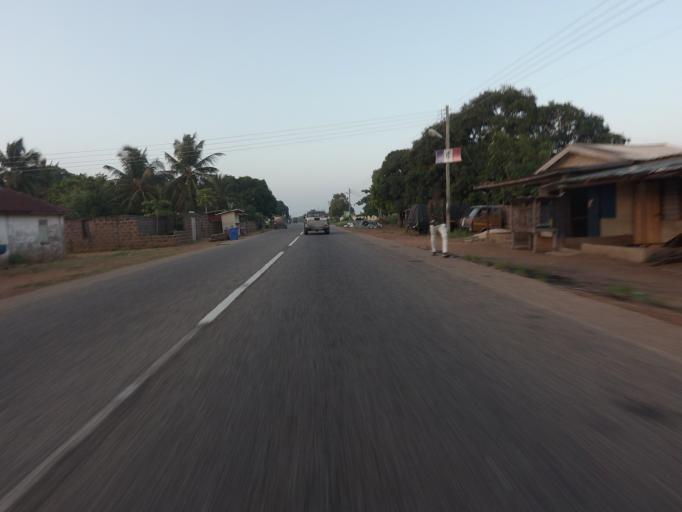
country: GH
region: Volta
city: Anloga
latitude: 5.8255
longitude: 0.9490
